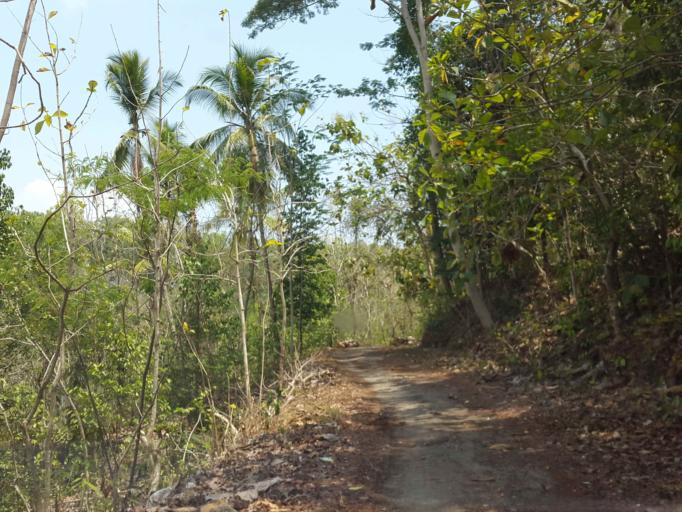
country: ID
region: East Java
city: Sudimoro
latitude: -8.2506
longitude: 111.2118
